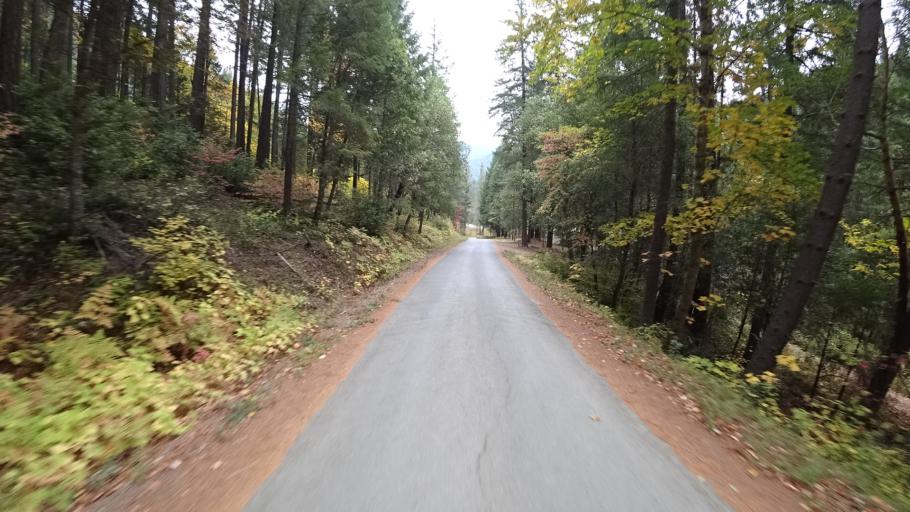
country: US
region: California
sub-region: Siskiyou County
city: Happy Camp
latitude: 41.8242
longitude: -123.3842
